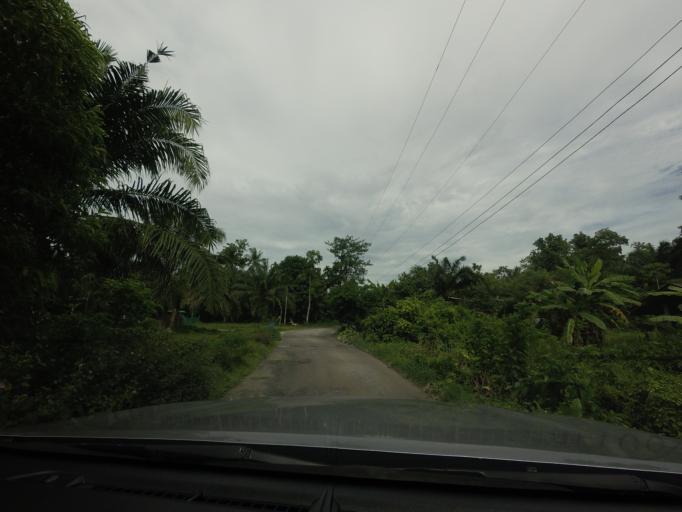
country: TH
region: Nakhon Si Thammarat
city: Phra Phrom
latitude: 8.2848
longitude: 99.9208
